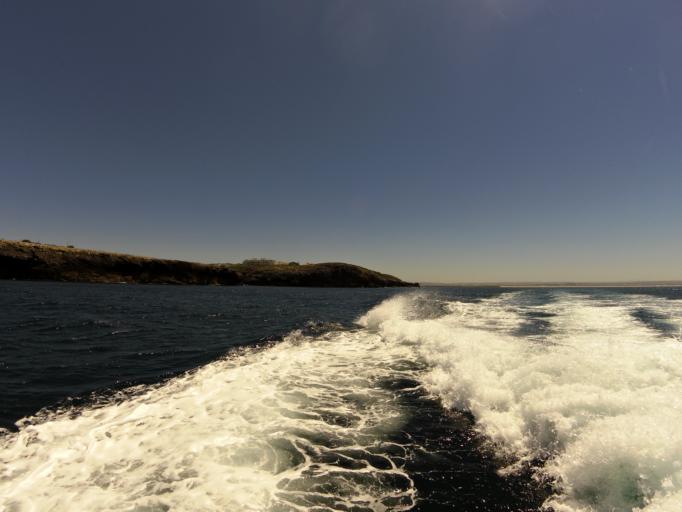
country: PT
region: Leiria
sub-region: Peniche
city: Peniche
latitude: 39.3531
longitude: -9.3984
